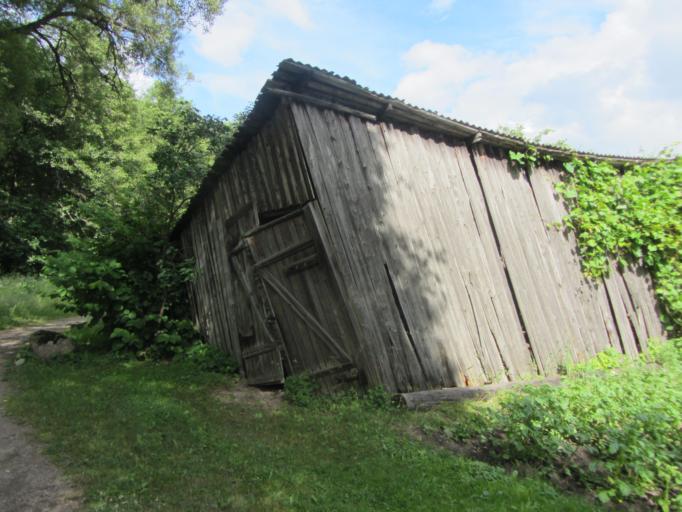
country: LT
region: Vilnius County
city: Rasos
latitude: 54.6898
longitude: 25.3595
